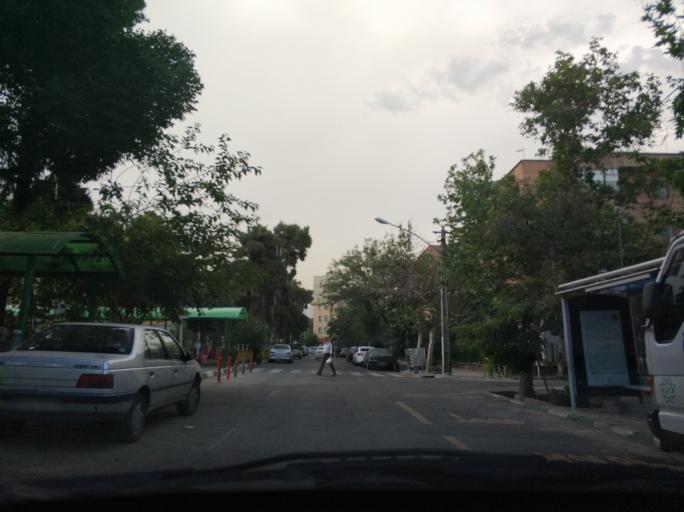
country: IR
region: Tehran
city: Tehran
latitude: 35.7187
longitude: 51.4745
